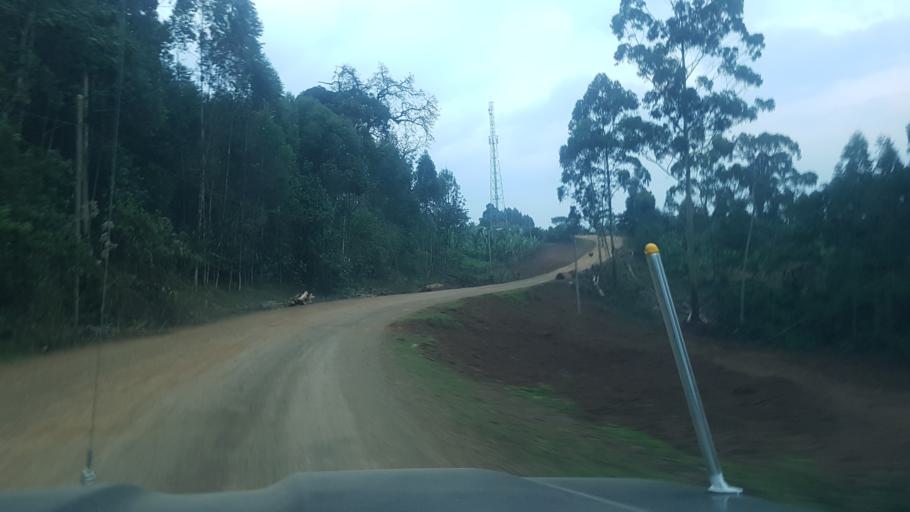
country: ET
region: Oromiya
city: Gore
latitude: 7.7863
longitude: 35.4594
